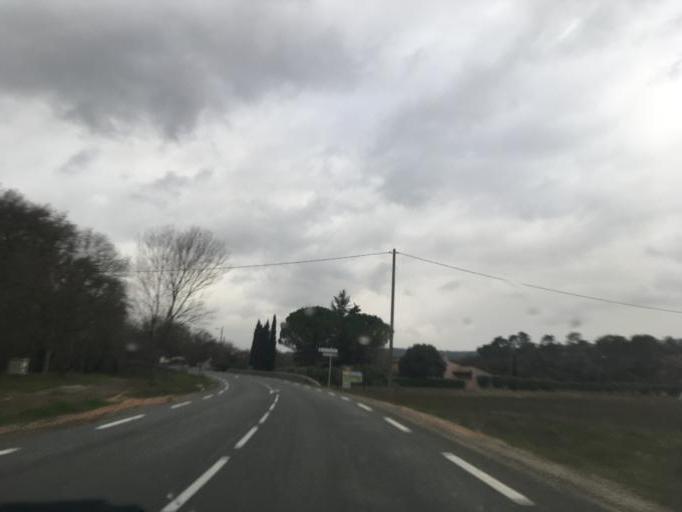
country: FR
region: Provence-Alpes-Cote d'Azur
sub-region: Departement du Var
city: Sainte-Anastasie-sur-Issole
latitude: 43.3396
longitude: 6.1362
